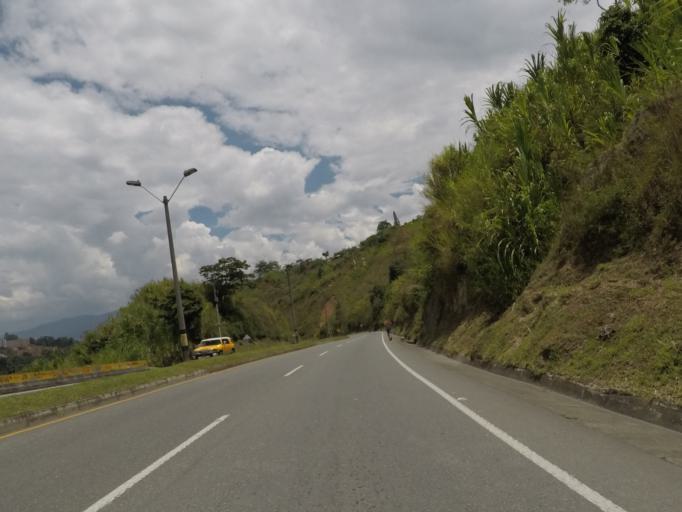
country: CO
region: Antioquia
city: Medellin
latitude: 6.2755
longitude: -75.6310
